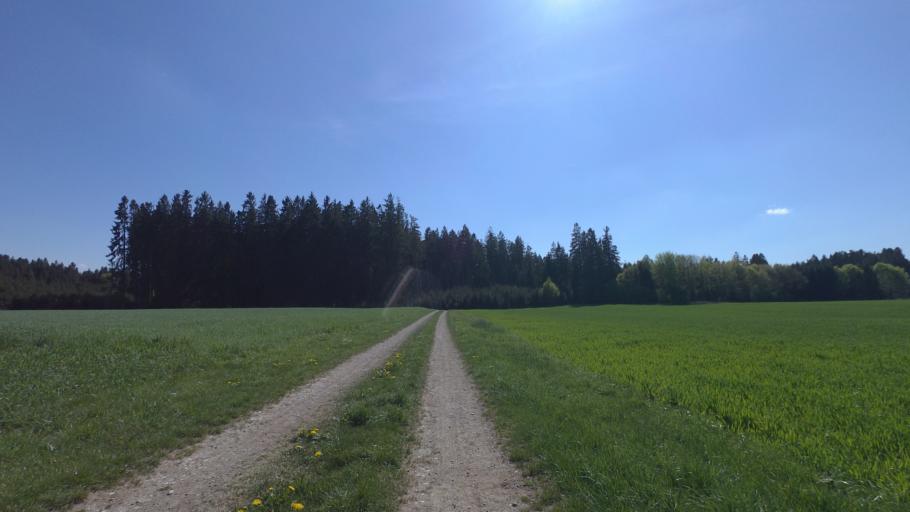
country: DE
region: Bavaria
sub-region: Upper Bavaria
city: Traunreut
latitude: 47.9533
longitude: 12.5391
